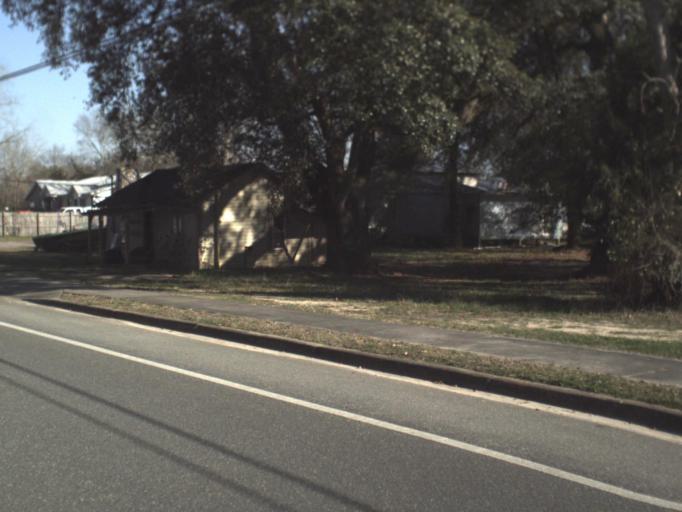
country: US
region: Florida
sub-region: Jackson County
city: Marianna
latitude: 30.7923
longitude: -85.3707
